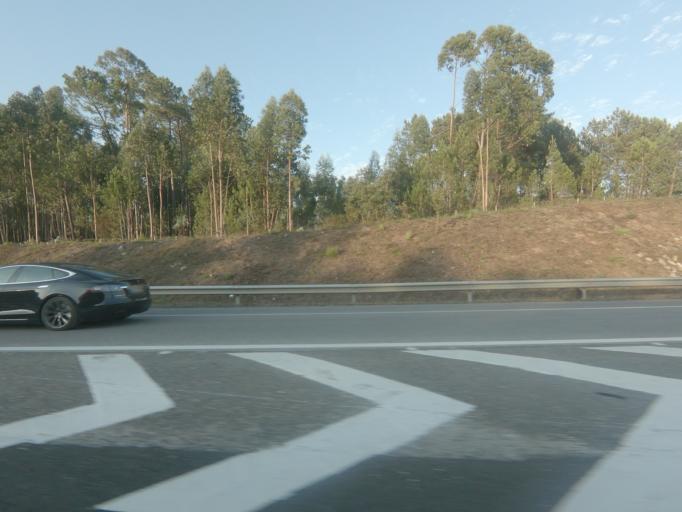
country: PT
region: Santarem
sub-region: Ourem
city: Fatima
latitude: 39.6256
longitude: -8.6958
